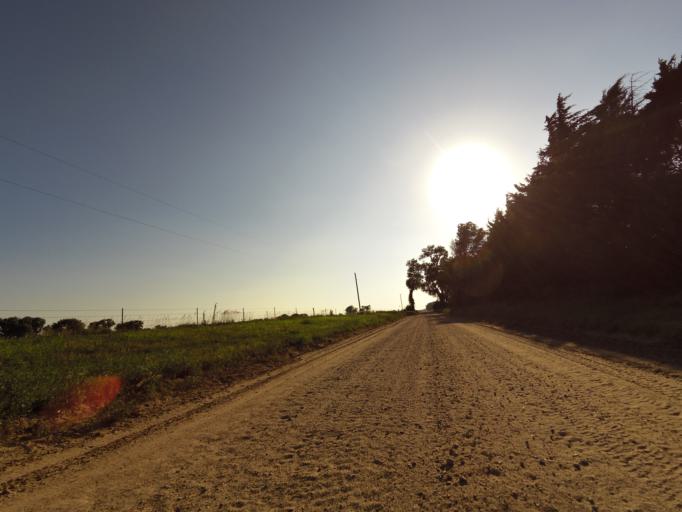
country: US
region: Kansas
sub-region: McPherson County
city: Inman
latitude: 38.1883
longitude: -97.8832
